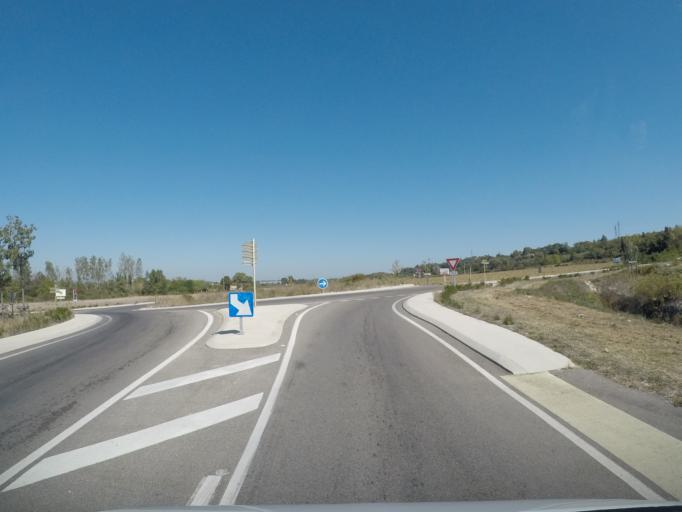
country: FR
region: Languedoc-Roussillon
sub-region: Departement du Gard
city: Uzes
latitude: 44.0033
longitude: 4.4015
